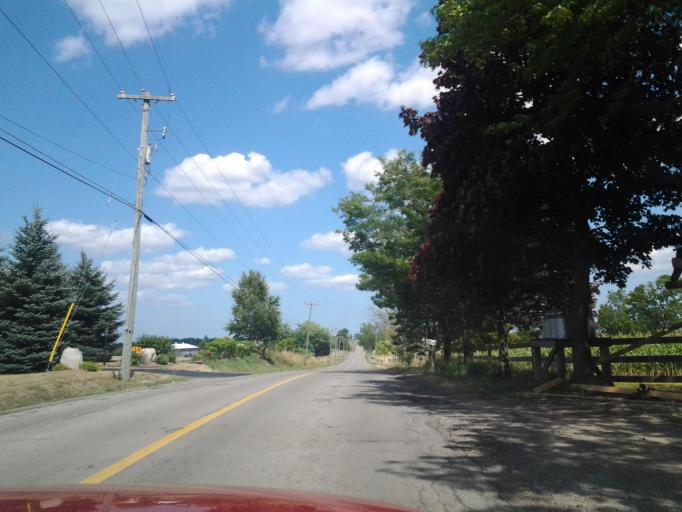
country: CA
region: Ontario
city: Ancaster
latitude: 43.2852
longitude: -79.9623
